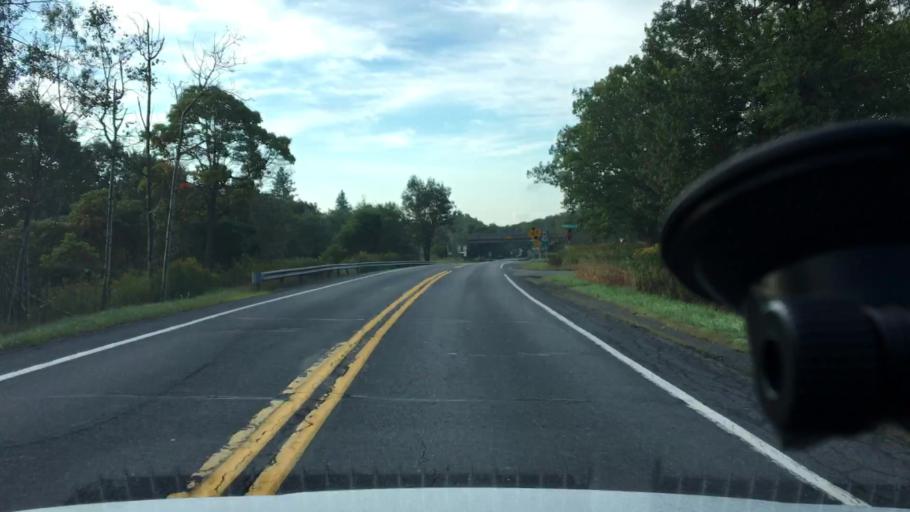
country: US
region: Pennsylvania
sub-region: Monroe County
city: Mount Pocono
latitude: 41.1129
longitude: -75.3867
